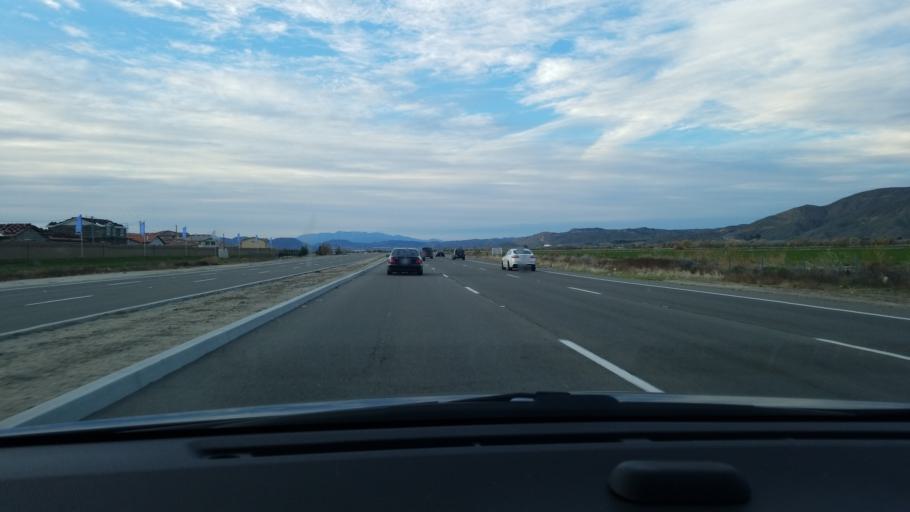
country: US
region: California
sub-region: Riverside County
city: San Jacinto
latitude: 33.8164
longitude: -116.9919
